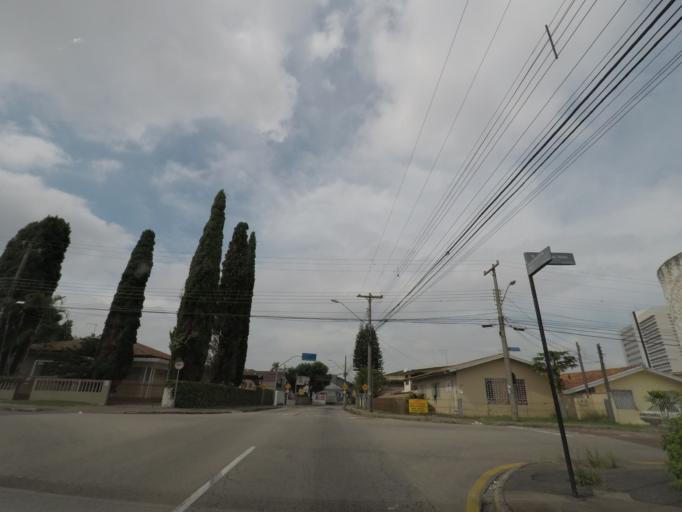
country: BR
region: Parana
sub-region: Curitiba
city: Curitiba
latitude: -25.4961
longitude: -49.2798
